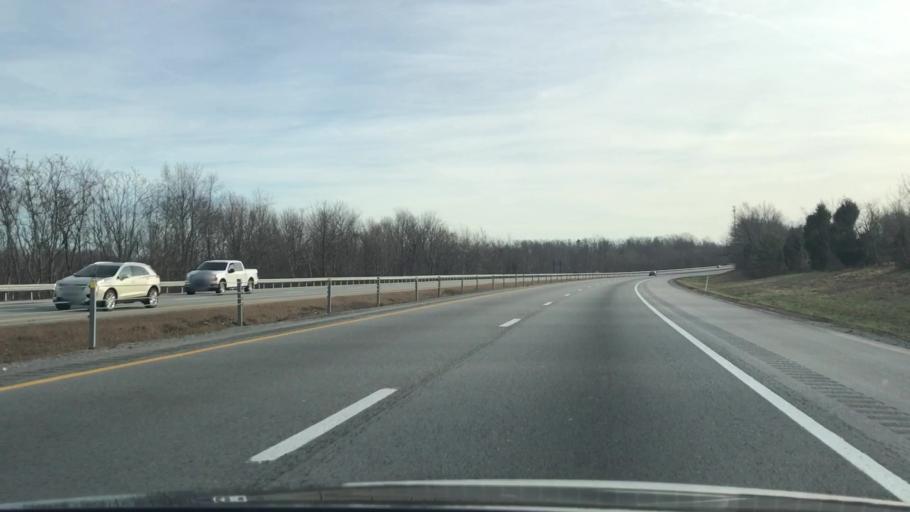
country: US
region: Tennessee
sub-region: Putnam County
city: Monterey
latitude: 36.1356
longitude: -85.3323
